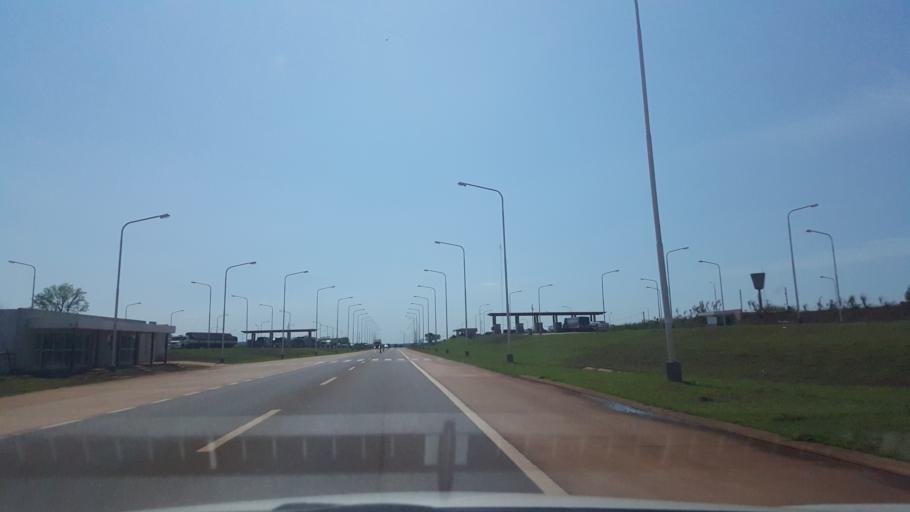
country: AR
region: Misiones
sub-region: Departamento de Apostoles
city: San Jose
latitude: -27.7832
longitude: -55.8203
